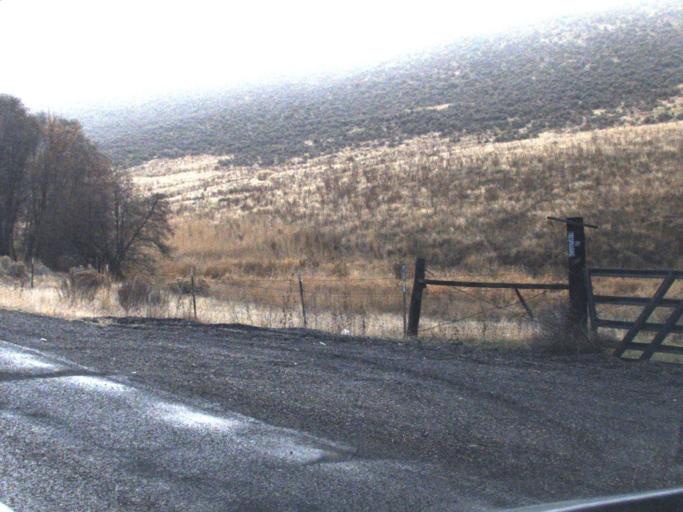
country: US
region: Washington
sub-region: Asotin County
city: Clarkston Heights-Vineland
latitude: 46.4142
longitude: -117.2727
